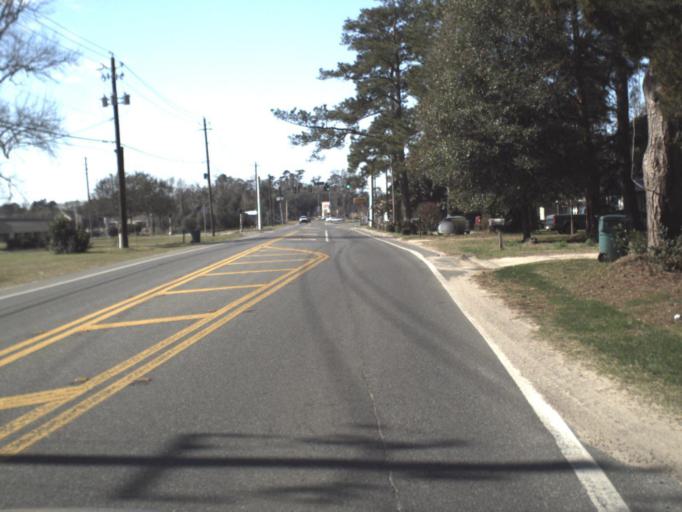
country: US
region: Florida
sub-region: Jackson County
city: Marianna
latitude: 30.7714
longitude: -85.2013
